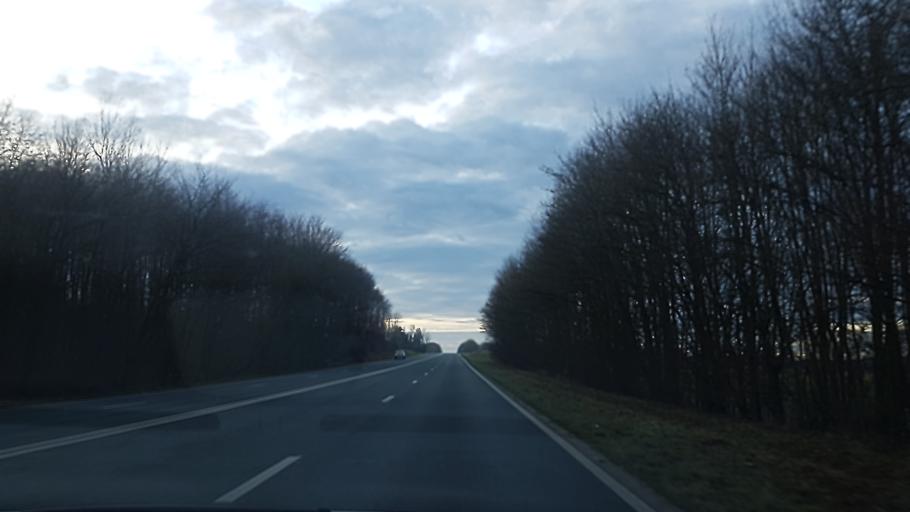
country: BE
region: Wallonia
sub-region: Province de Namur
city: Couvin
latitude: 50.0517
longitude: 4.4681
